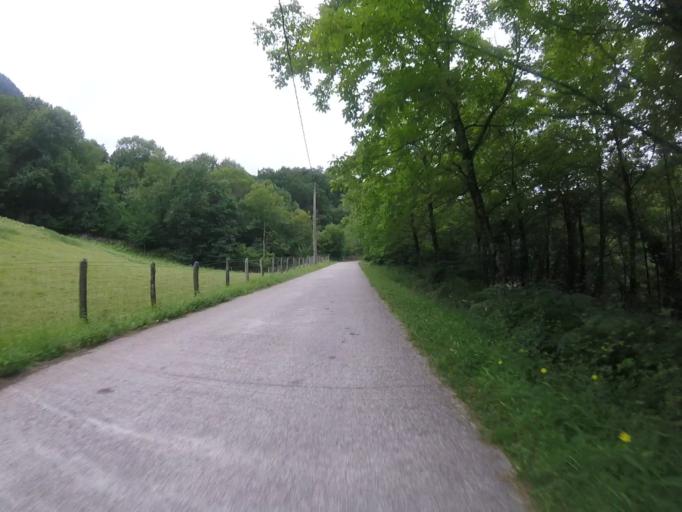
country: ES
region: Navarre
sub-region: Provincia de Navarra
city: Doneztebe
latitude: 43.1485
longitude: -1.6690
